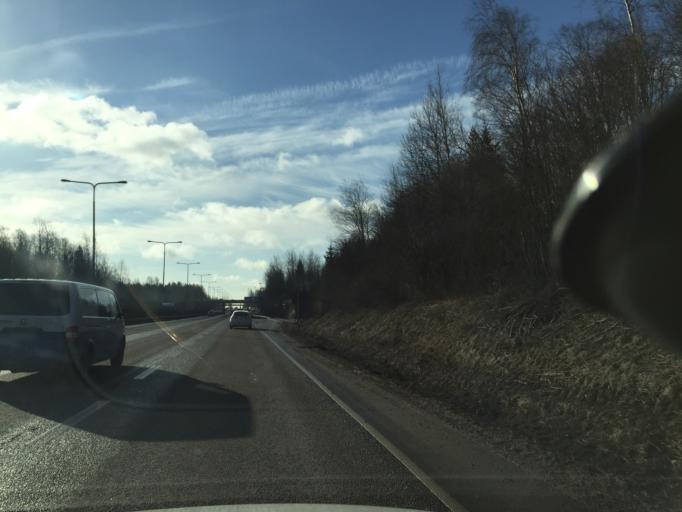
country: FI
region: Uusimaa
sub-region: Helsinki
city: Teekkarikylae
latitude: 60.2389
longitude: 24.8963
